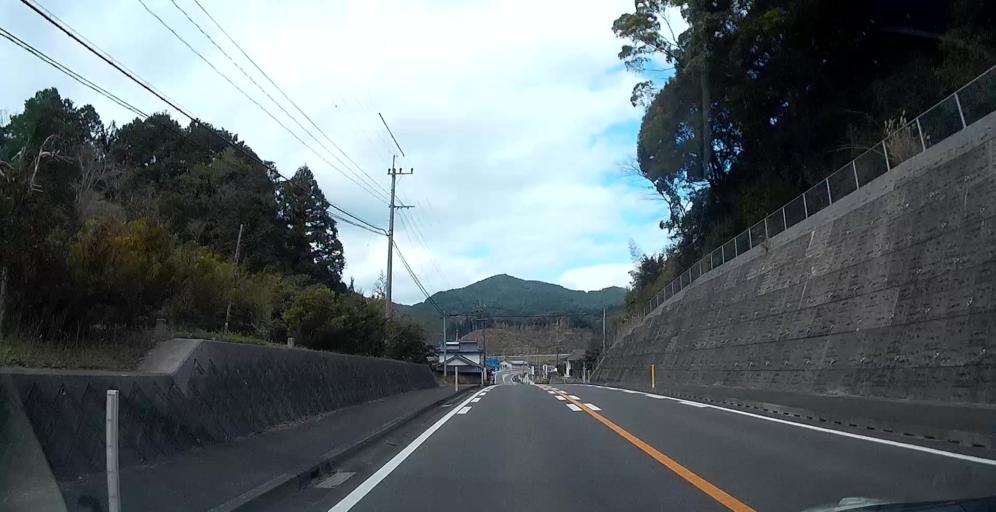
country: JP
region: Kumamoto
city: Minamata
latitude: 32.2362
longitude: 130.4655
